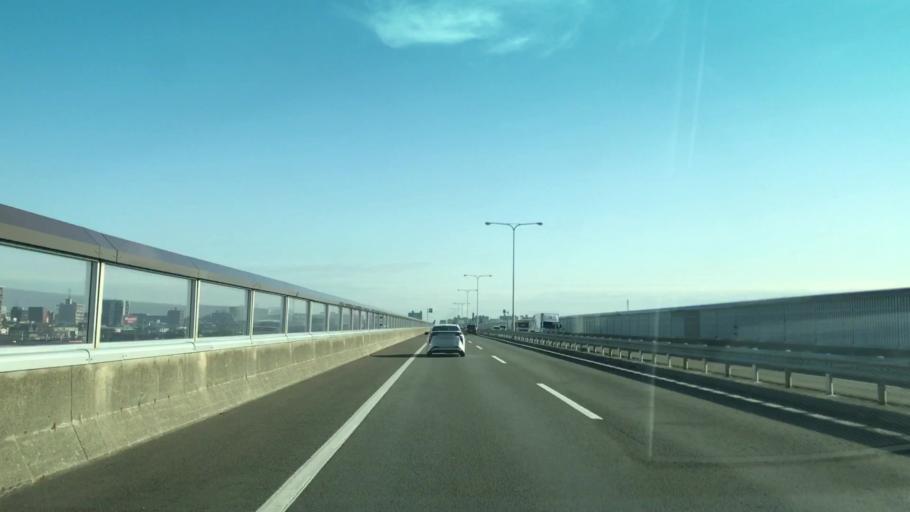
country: JP
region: Hokkaido
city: Sapporo
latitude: 43.1019
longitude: 141.3488
